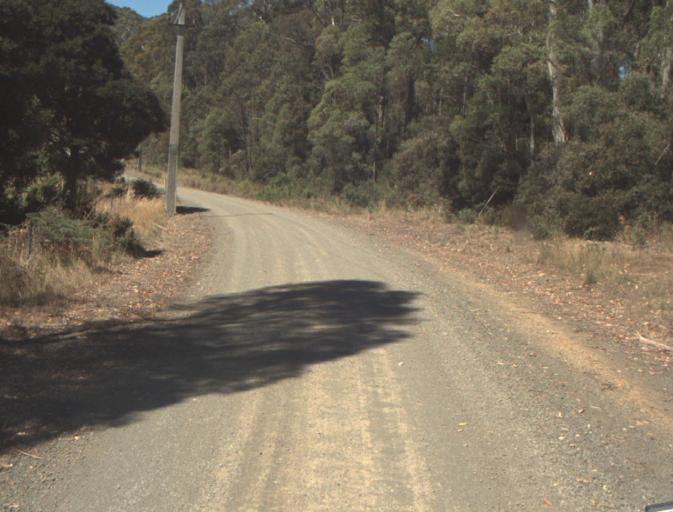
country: AU
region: Tasmania
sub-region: Launceston
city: Newstead
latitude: -41.3435
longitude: 147.3686
